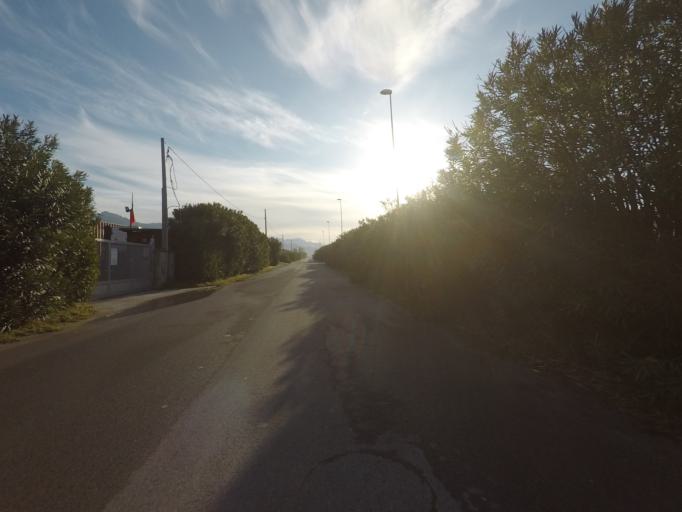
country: IT
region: Tuscany
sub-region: Provincia di Massa-Carrara
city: Massa
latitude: 44.0327
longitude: 10.1024
